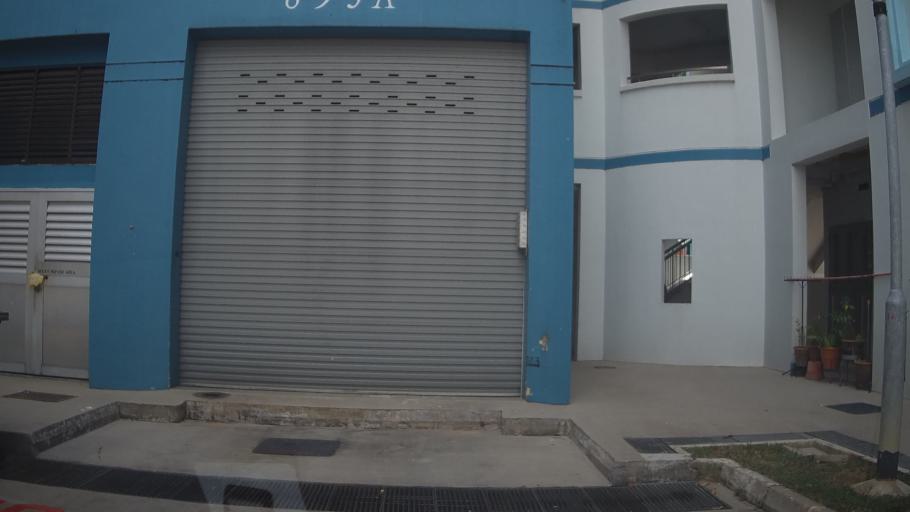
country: SG
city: Singapore
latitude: 1.3485
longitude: 103.9307
